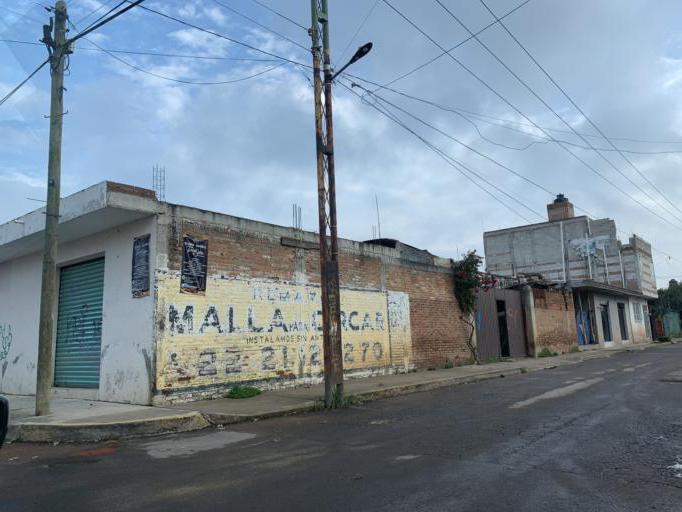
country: MX
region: Puebla
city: Cholula
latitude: 19.0739
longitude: -98.3065
